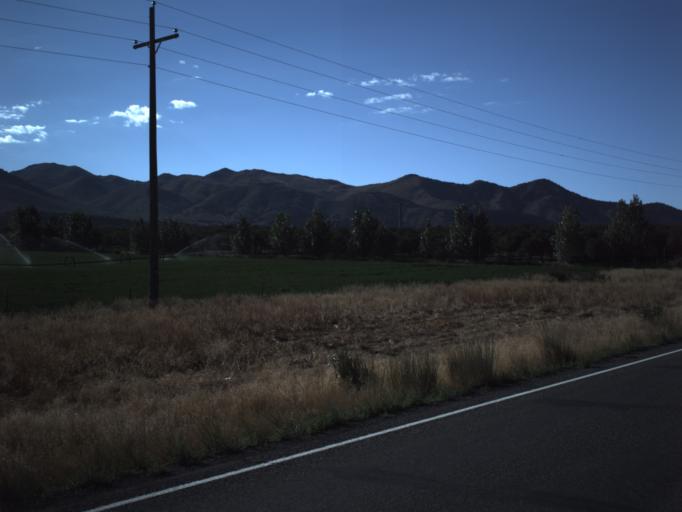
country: US
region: Utah
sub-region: Juab County
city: Mona
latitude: 39.8834
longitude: -112.1380
